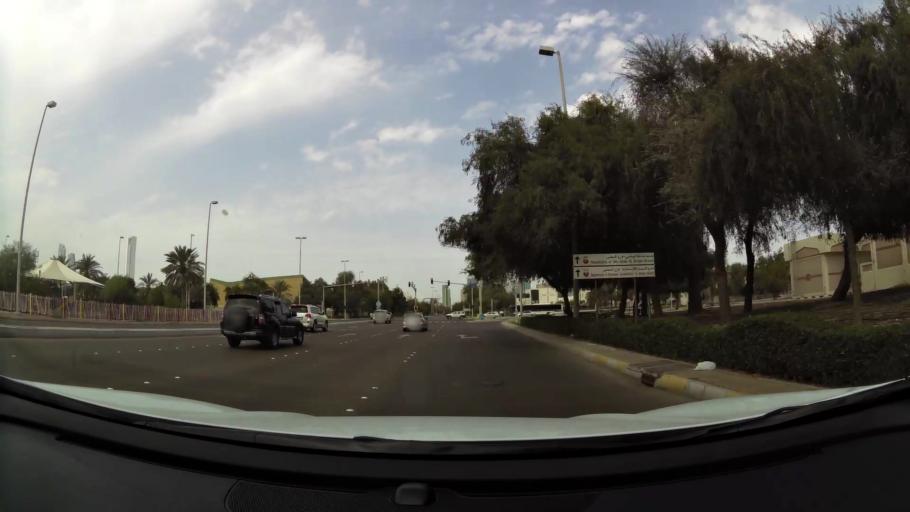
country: AE
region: Abu Dhabi
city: Abu Dhabi
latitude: 24.4598
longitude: 54.3467
